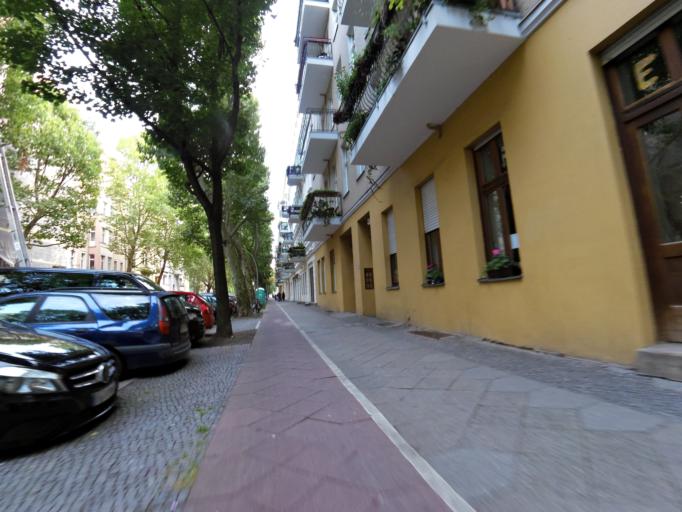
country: DE
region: Berlin
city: Berlin Schoeneberg
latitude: 52.4933
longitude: 13.3550
